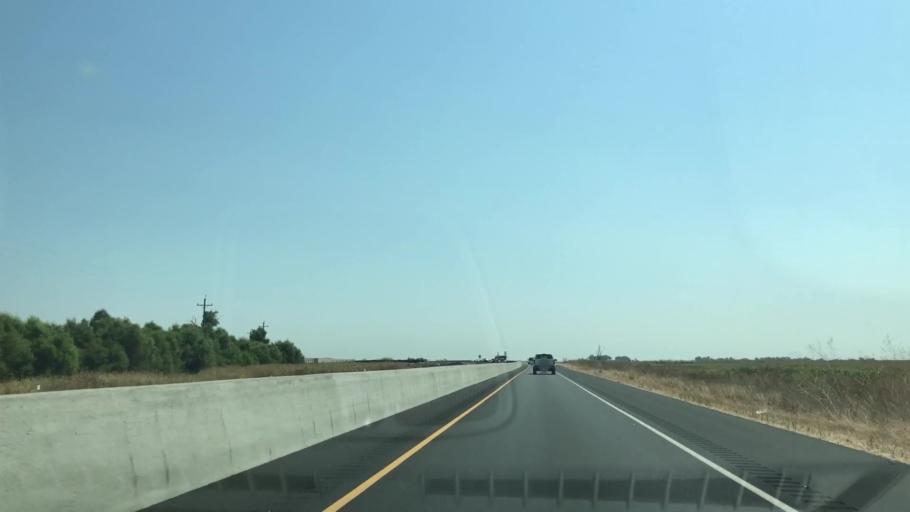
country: US
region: California
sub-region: Contra Costa County
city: Bethel Island
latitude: 38.1157
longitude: -121.5571
